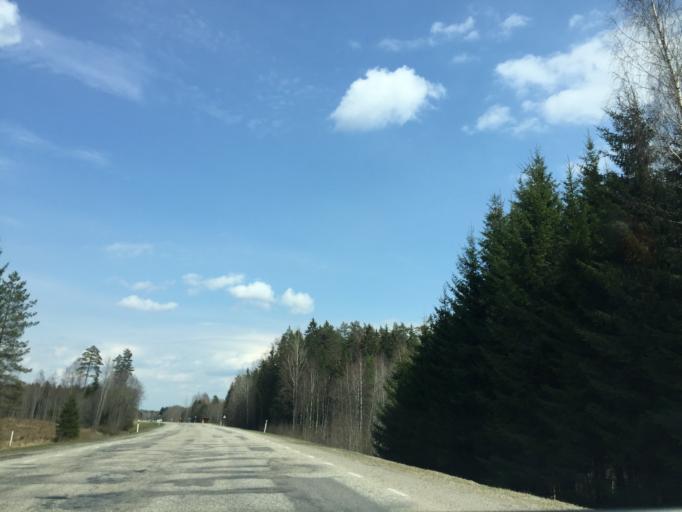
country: LV
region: Aluksnes Rajons
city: Aluksne
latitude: 57.5862
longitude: 27.0717
